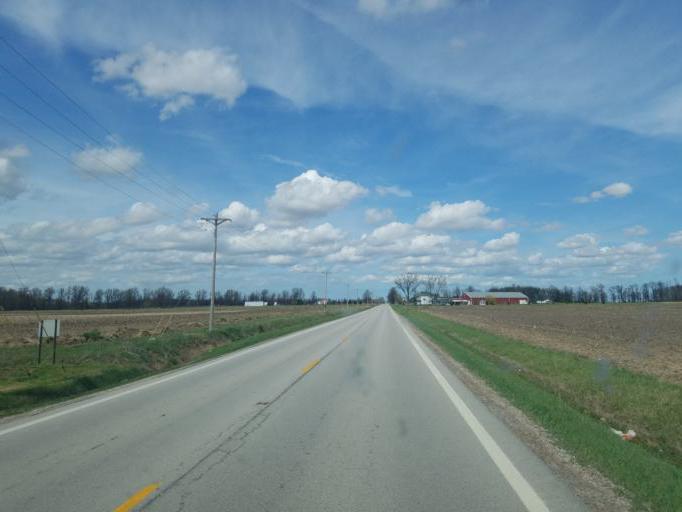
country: US
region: Ohio
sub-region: Huron County
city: Bellevue
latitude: 41.2082
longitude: -82.8208
